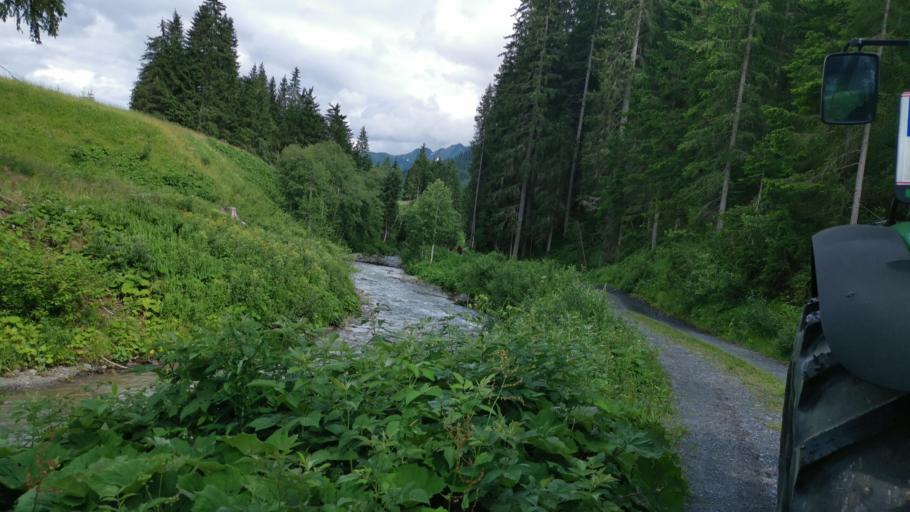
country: AT
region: Tyrol
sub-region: Politischer Bezirk Lienz
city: Obertilliach
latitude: 46.7052
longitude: 12.6001
